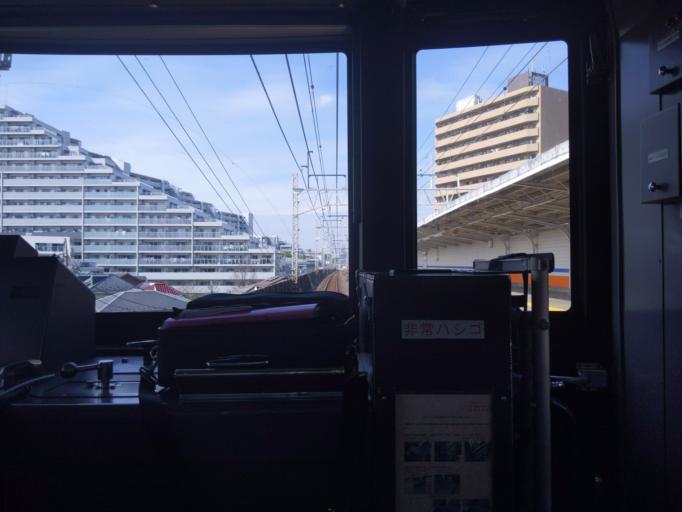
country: JP
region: Saitama
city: Soka
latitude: 35.7727
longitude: 139.7973
